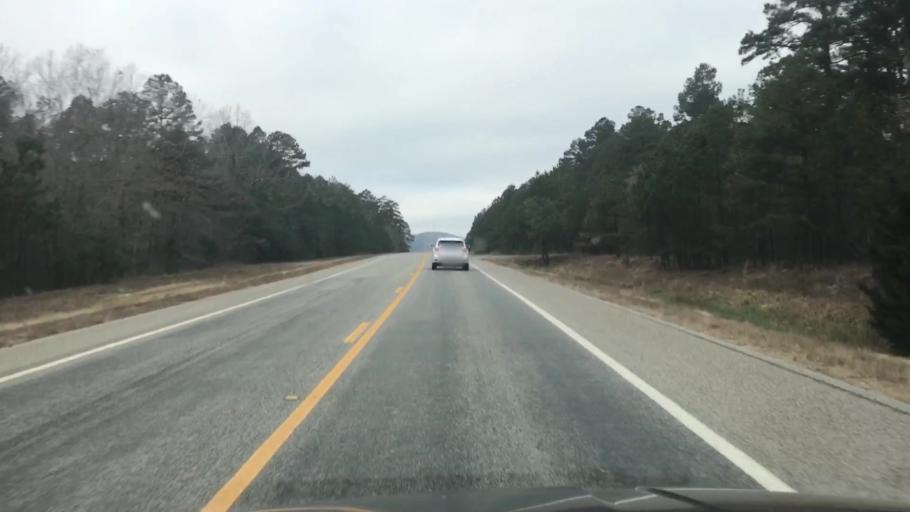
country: US
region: Arkansas
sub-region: Montgomery County
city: Mount Ida
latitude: 34.6874
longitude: -93.8801
